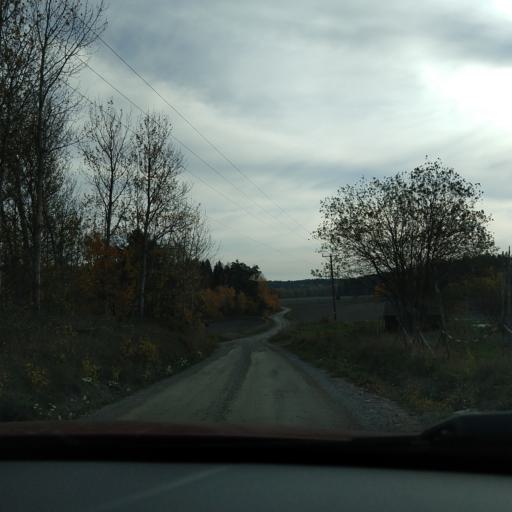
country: SE
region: Stockholm
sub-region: Vallentuna Kommun
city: Vallentuna
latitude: 59.5420
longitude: 18.0176
